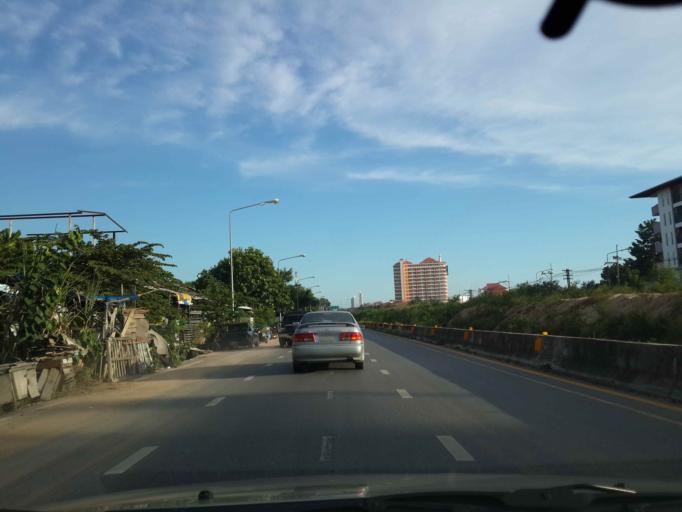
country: TH
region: Chon Buri
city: Phatthaya
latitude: 12.9152
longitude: 100.9022
